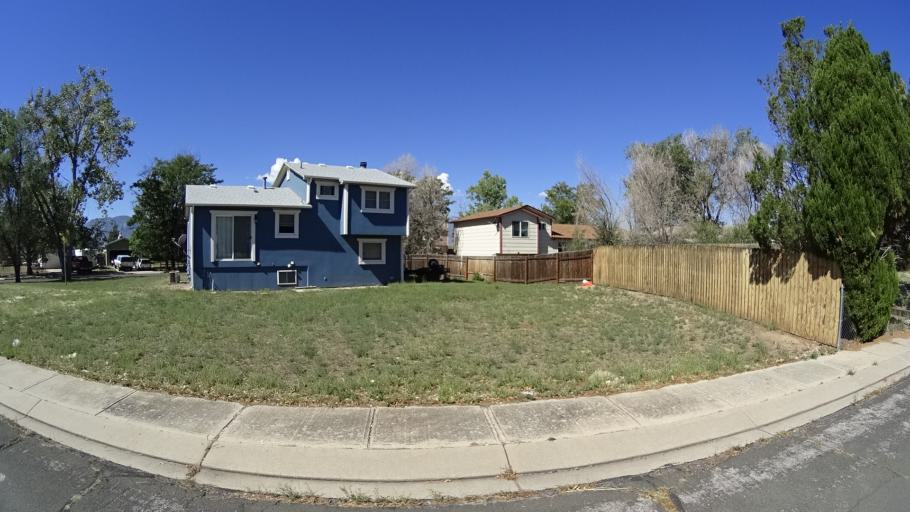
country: US
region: Colorado
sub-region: El Paso County
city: Stratmoor
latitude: 38.8146
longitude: -104.7382
